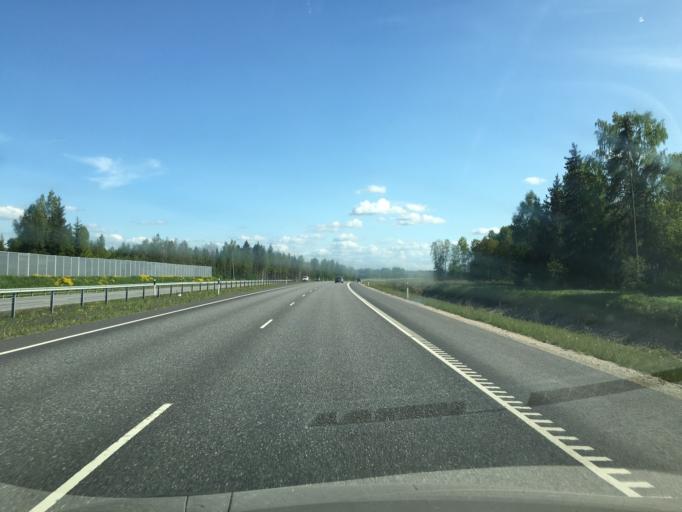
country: EE
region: Harju
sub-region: Rae vald
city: Vaida
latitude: 59.2424
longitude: 25.0255
